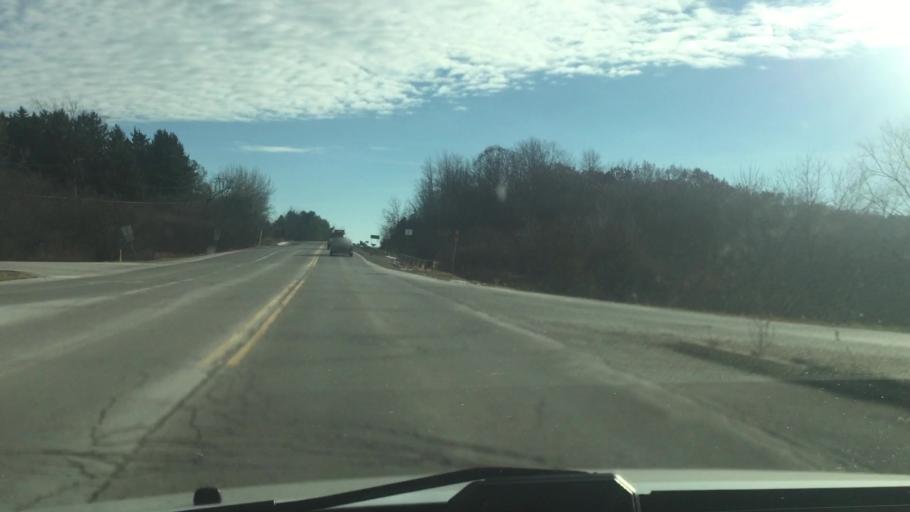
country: US
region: Wisconsin
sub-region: Waukesha County
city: Delafield
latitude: 43.0531
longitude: -88.4048
